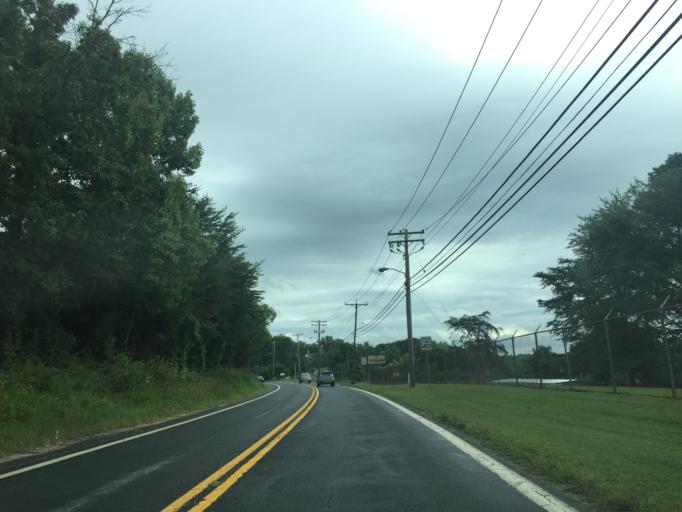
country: US
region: Maryland
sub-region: Baltimore County
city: White Marsh
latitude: 39.3797
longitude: -76.4351
